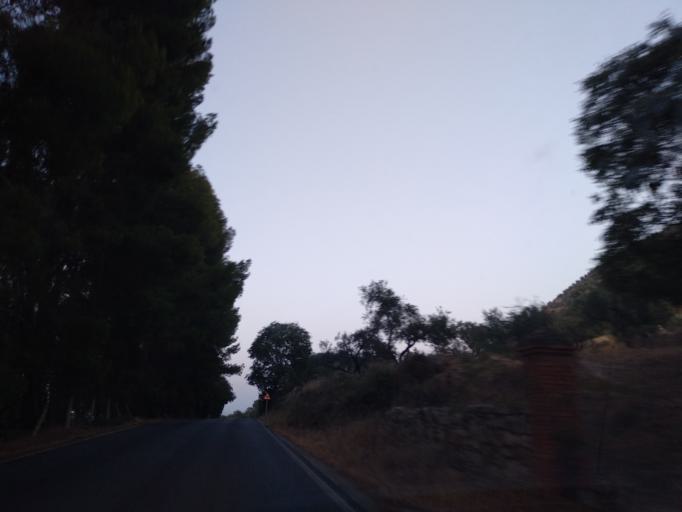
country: ES
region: Andalusia
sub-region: Provincia de Malaga
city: Cartama
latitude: 36.7032
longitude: -4.6433
